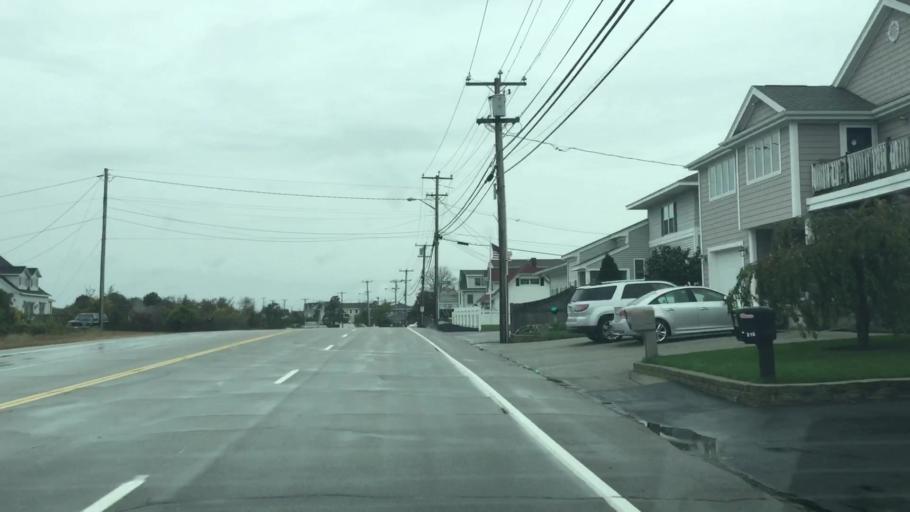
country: US
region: New Hampshire
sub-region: Rockingham County
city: Hampton Beach
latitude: 42.8793
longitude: -70.8182
